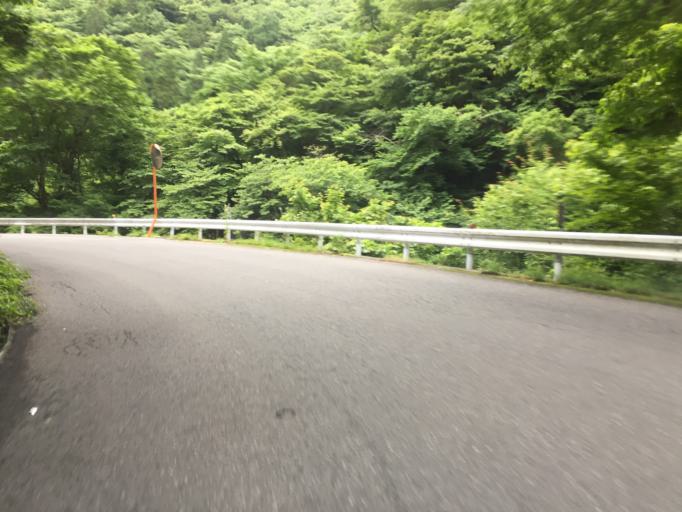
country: JP
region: Fukushima
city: Namie
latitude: 37.6845
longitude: 140.8694
